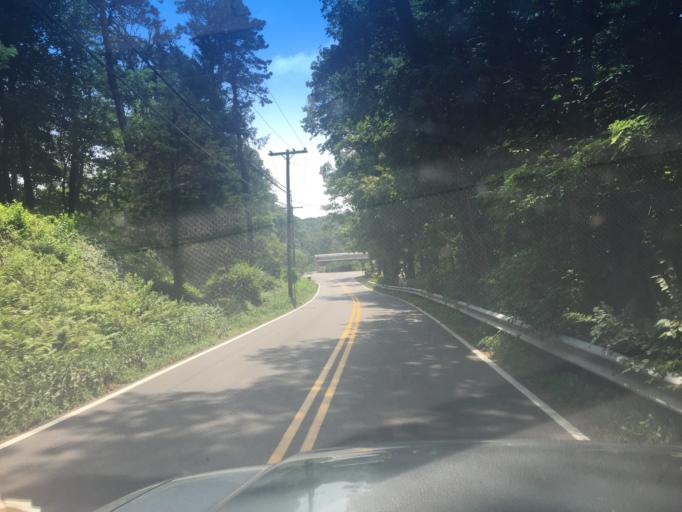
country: US
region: Massachusetts
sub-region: Barnstable County
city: Falmouth
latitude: 41.5742
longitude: -70.6271
